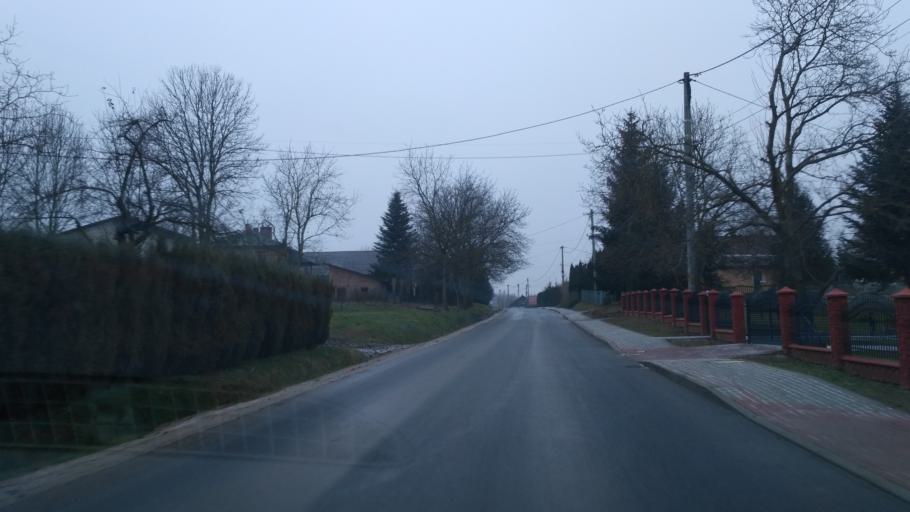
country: PL
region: Subcarpathian Voivodeship
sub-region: Powiat przeworski
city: Kanczuga
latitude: 50.0165
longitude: 22.4074
